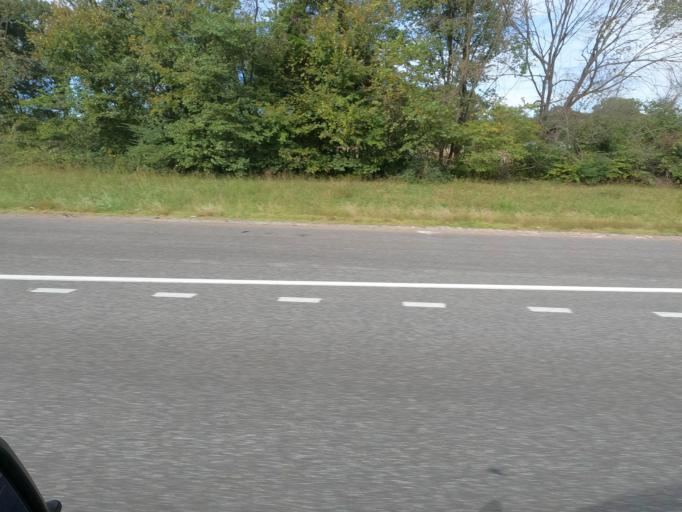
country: US
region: Tennessee
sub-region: Haywood County
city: Brownsville
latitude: 35.4755
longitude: -89.2777
